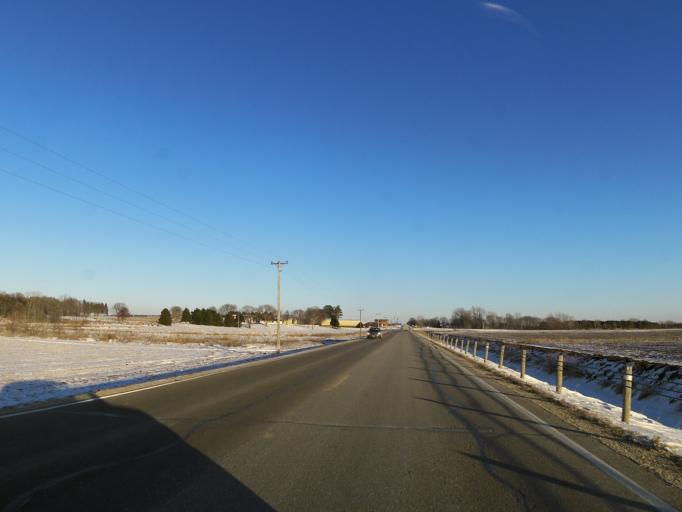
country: US
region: Minnesota
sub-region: Rice County
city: Northfield
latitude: 44.5437
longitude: -93.1428
